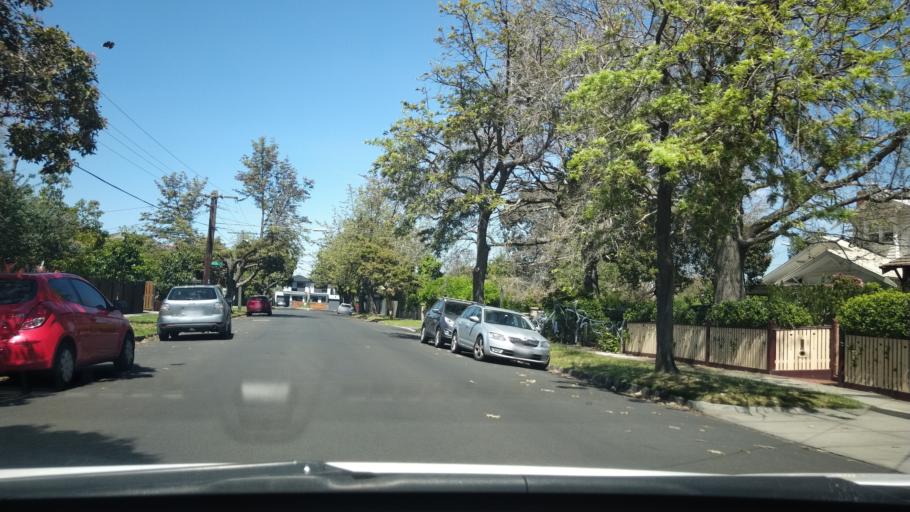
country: AU
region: Victoria
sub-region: Glen Eira
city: Glen Huntly
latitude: -37.8918
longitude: 145.0402
